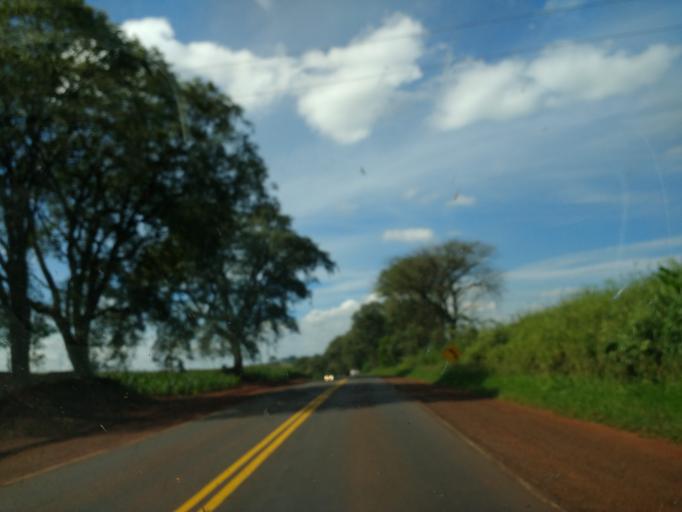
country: BR
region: Parana
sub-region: Engenheiro Beltrao
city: Engenheiro Beltrao
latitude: -23.5661
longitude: -52.2538
